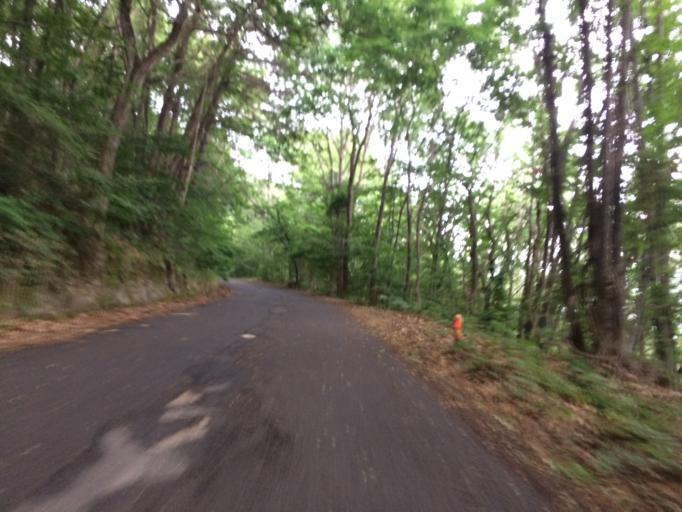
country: IT
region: Liguria
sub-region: Provincia di Imperia
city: Triora
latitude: 43.9834
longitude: 7.7548
